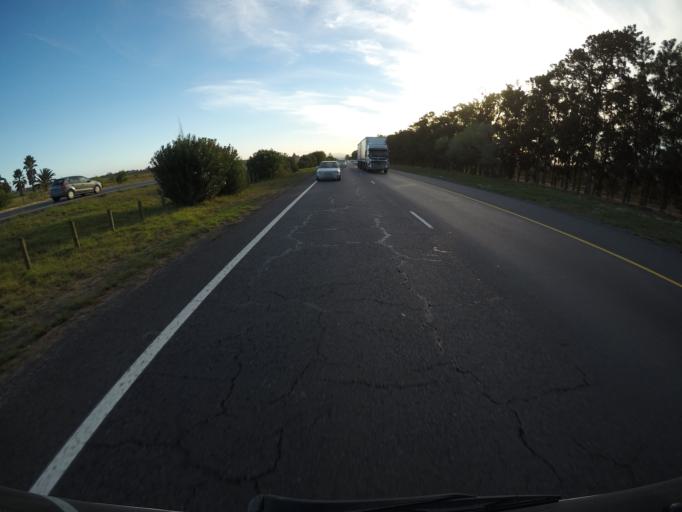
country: ZA
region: Western Cape
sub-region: City of Cape Town
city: Kraaifontein
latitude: -33.8249
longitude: 18.7734
